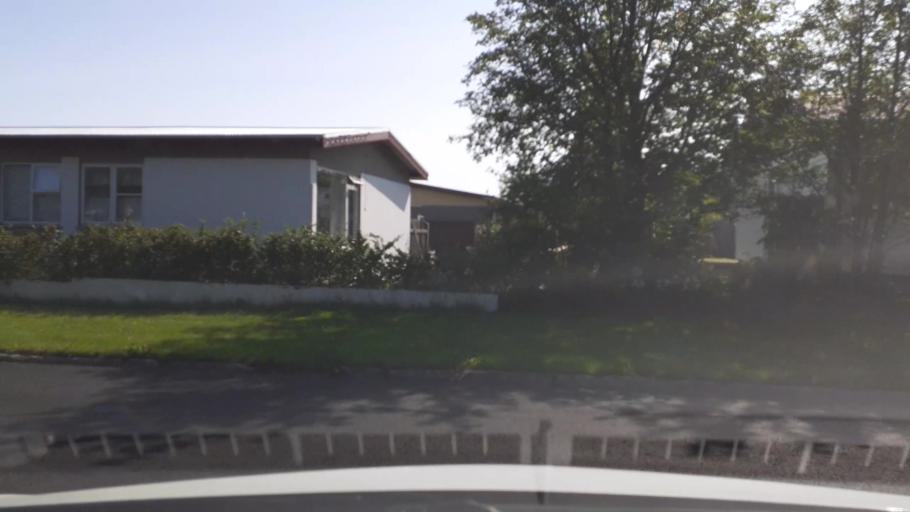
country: IS
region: South
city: Hveragerdi
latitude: 64.0038
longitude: -21.2029
